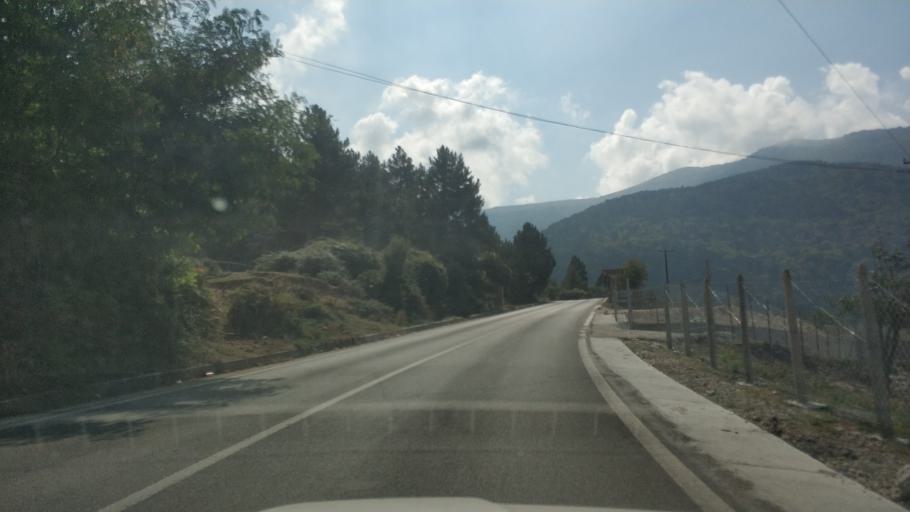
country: AL
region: Vlore
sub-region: Rrethi i Vlores
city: Brataj
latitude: 40.2295
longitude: 19.5783
